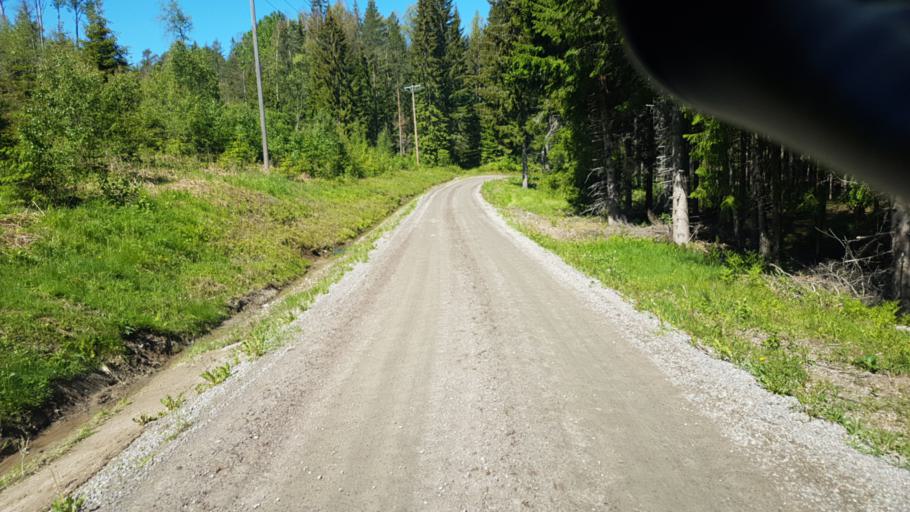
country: SE
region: Vaermland
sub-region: Grums Kommun
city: Grums
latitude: 59.4971
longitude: 12.9258
